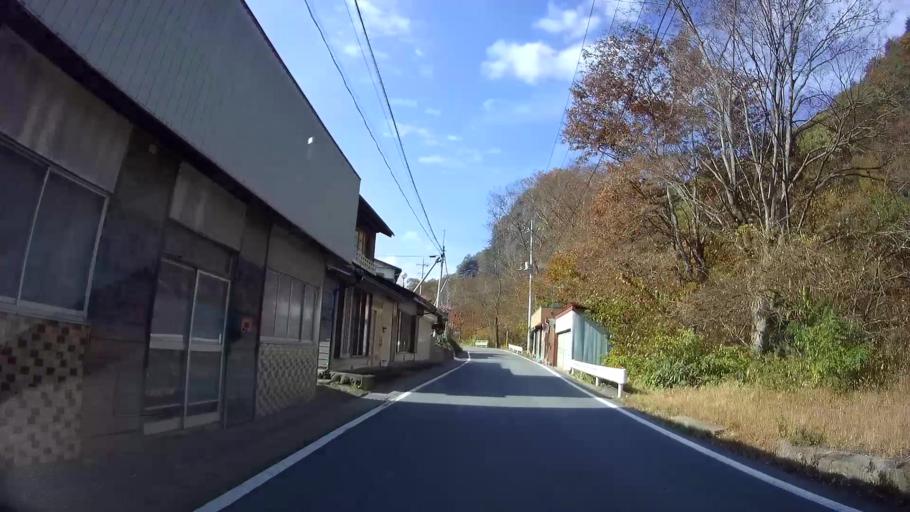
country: JP
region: Gunma
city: Nakanojomachi
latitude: 36.5137
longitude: 138.7725
